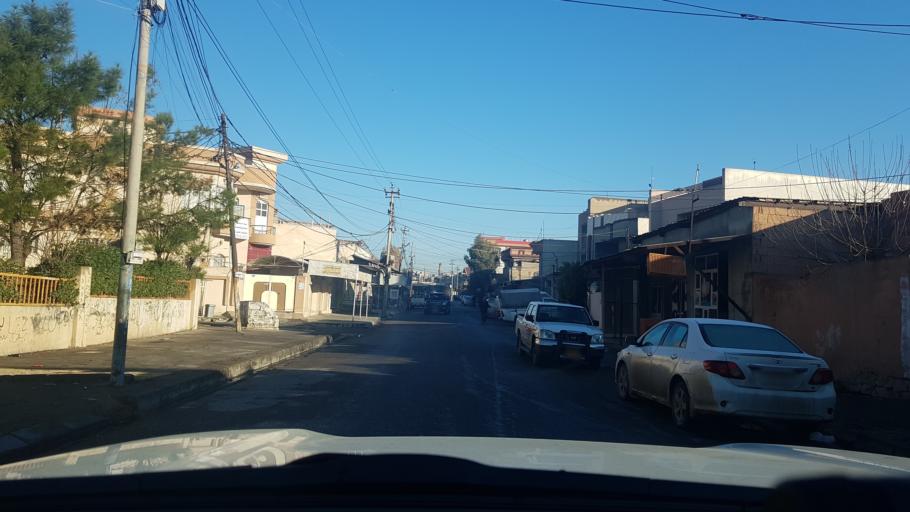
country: IQ
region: Arbil
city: Erbil
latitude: 36.2052
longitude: 44.0086
